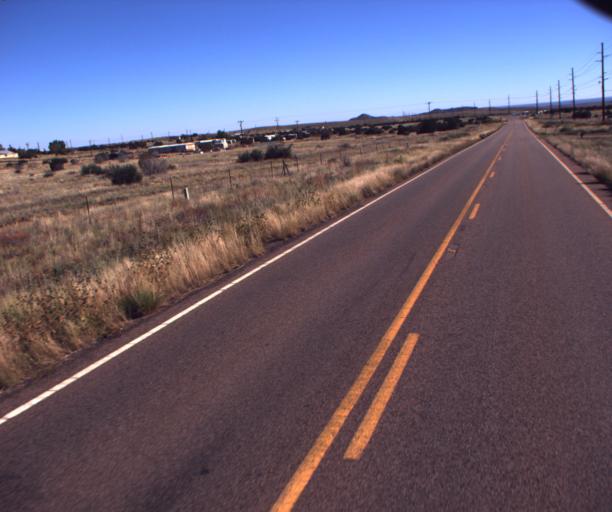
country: US
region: Arizona
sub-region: Navajo County
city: Taylor
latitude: 34.4848
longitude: -110.2505
